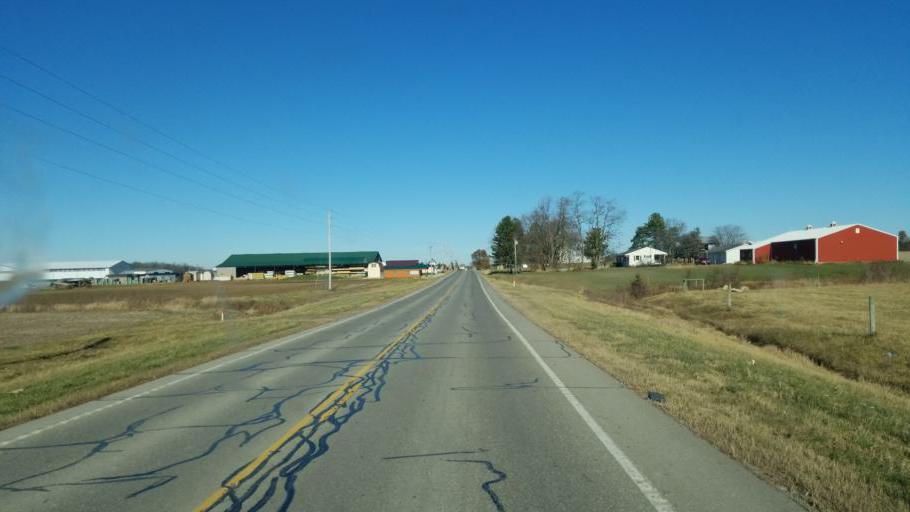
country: US
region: Ohio
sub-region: Huron County
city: Greenwich
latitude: 40.9560
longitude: -82.4951
